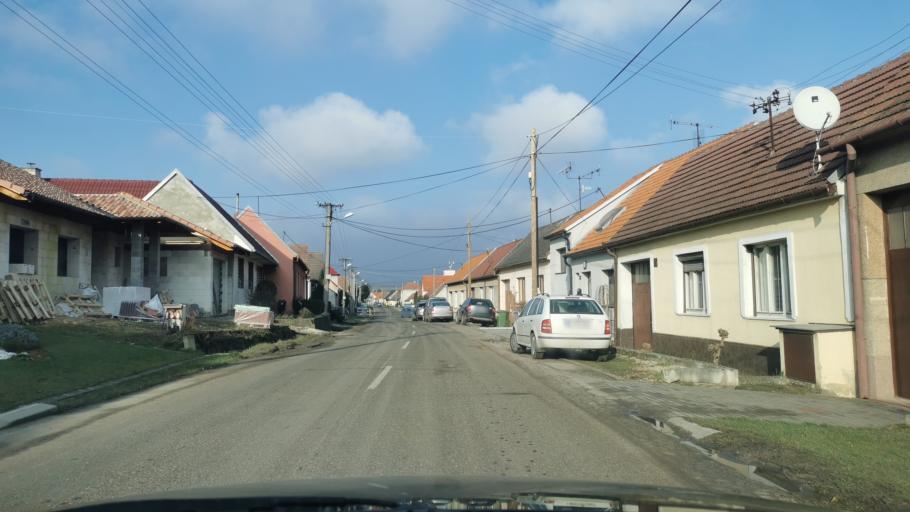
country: SK
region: Trnavsky
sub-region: Okres Skalica
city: Skalica
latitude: 48.7627
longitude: 17.2820
